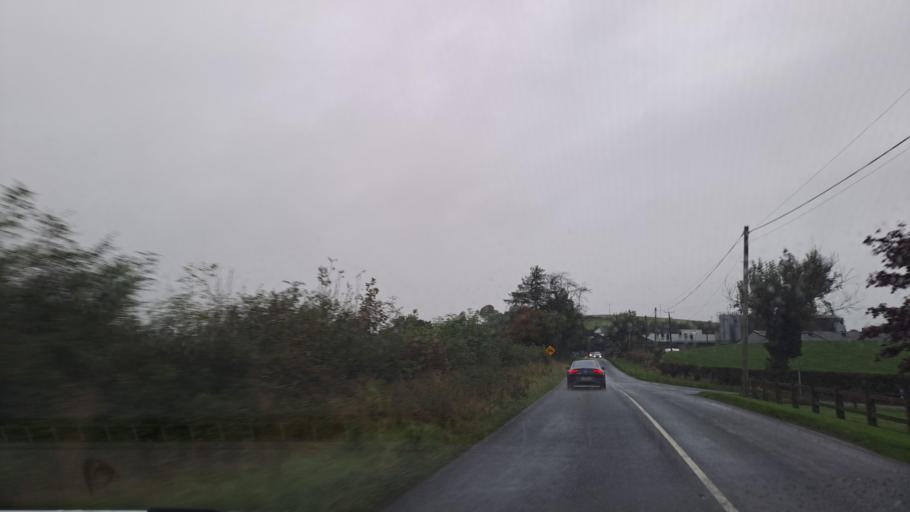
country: IE
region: Ulster
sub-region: County Monaghan
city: Monaghan
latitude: 54.2211
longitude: -6.9191
